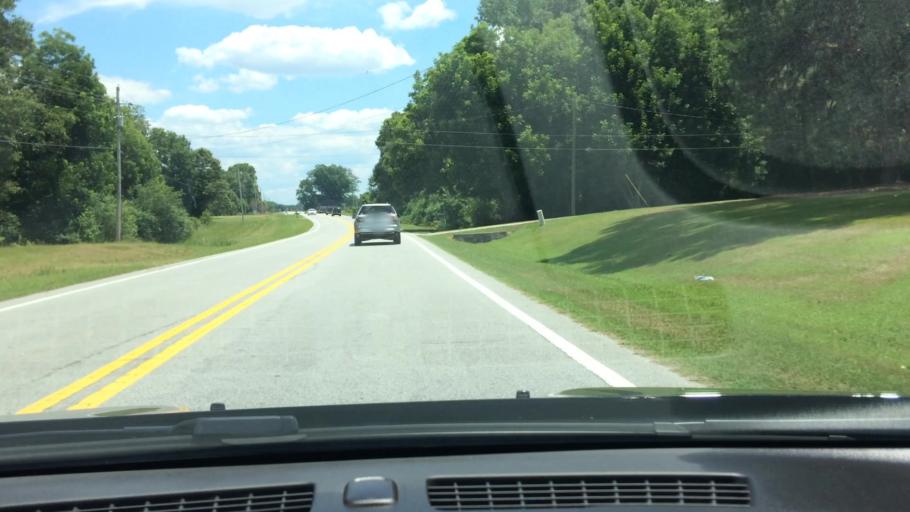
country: US
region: North Carolina
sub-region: Pitt County
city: Summerfield
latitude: 35.6316
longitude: -77.4423
